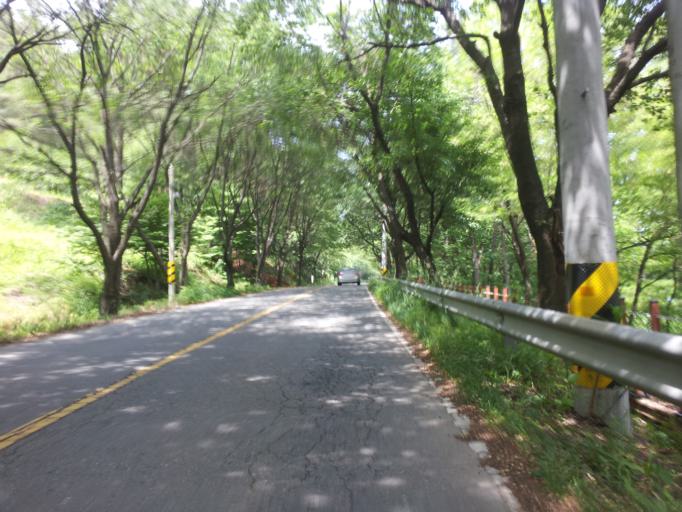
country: KR
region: Daejeon
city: Sintansin
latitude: 36.4333
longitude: 127.4689
